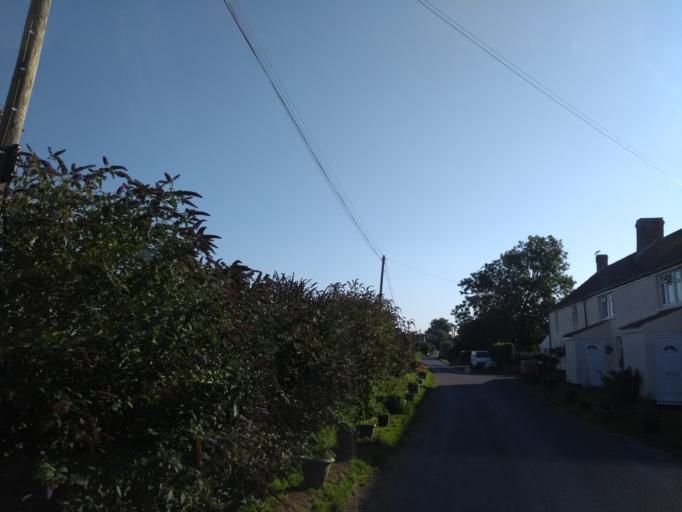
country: GB
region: England
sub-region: Somerset
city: Westonzoyland
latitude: 51.1301
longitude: -2.9503
